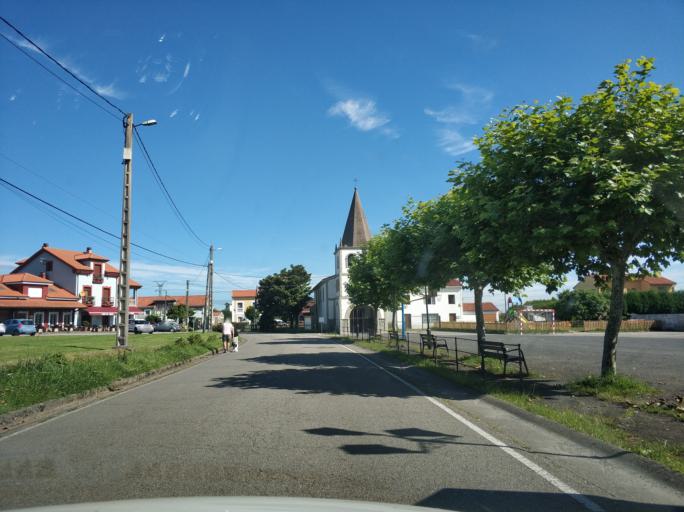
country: ES
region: Asturias
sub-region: Province of Asturias
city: Cudillero
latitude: 43.5746
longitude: -6.2385
